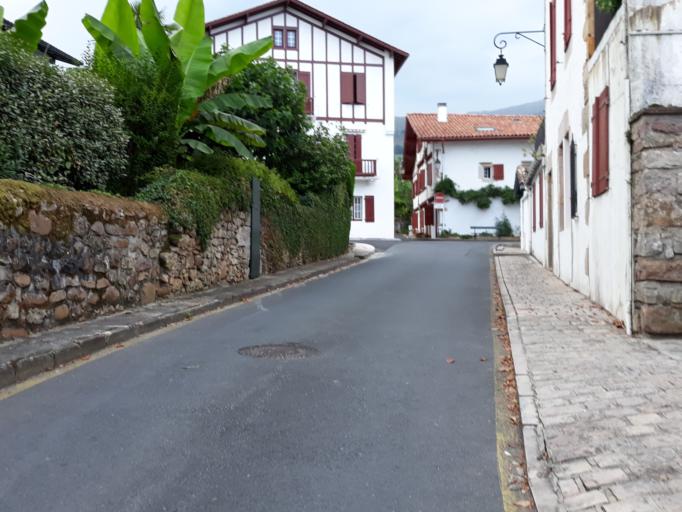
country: FR
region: Aquitaine
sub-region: Departement des Pyrenees-Atlantiques
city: Ascain
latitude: 43.3456
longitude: -1.6219
